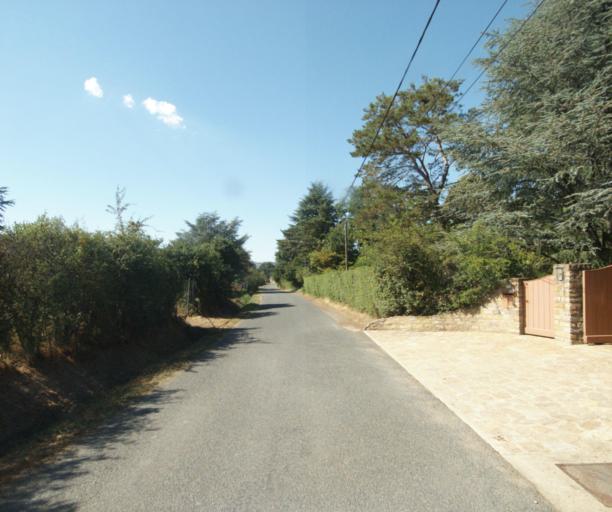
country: FR
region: Rhone-Alpes
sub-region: Departement du Rhone
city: Lozanne
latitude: 45.8376
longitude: 4.7058
